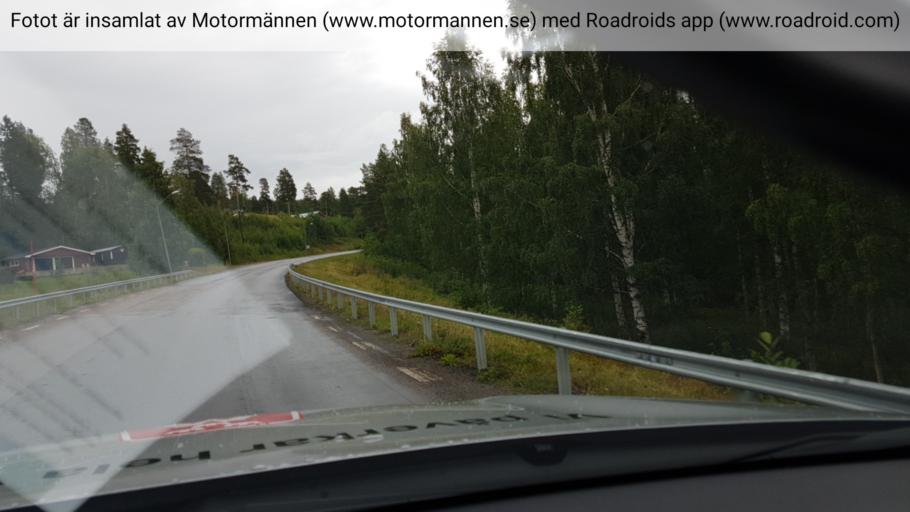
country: SE
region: Norrbotten
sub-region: Alvsbyns Kommun
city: AElvsbyn
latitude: 66.0927
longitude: 20.9381
